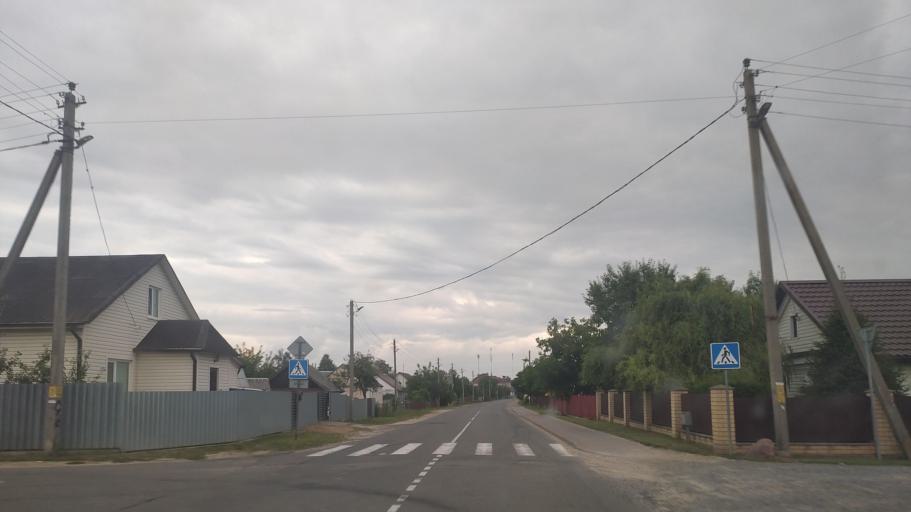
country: BY
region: Brest
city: Byaroza
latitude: 52.5238
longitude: 24.9734
